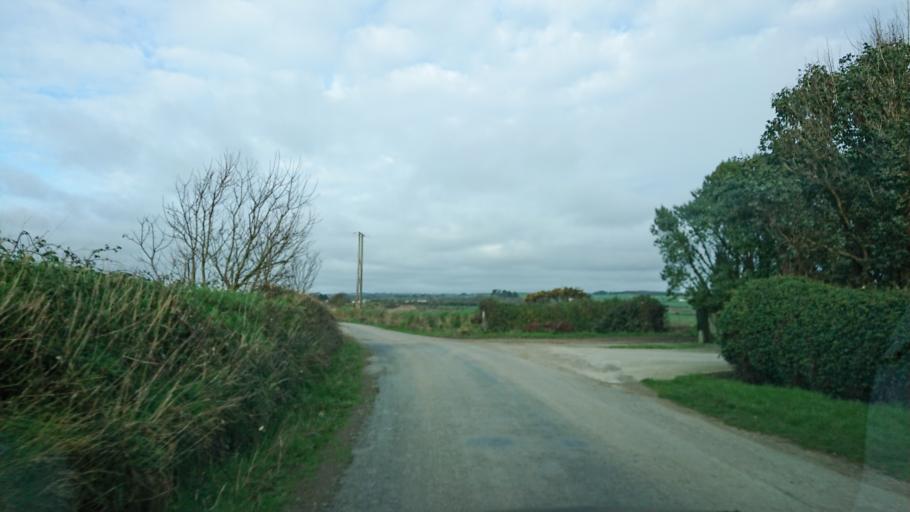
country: IE
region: Munster
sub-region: Waterford
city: Portlaw
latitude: 52.1445
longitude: -7.3052
